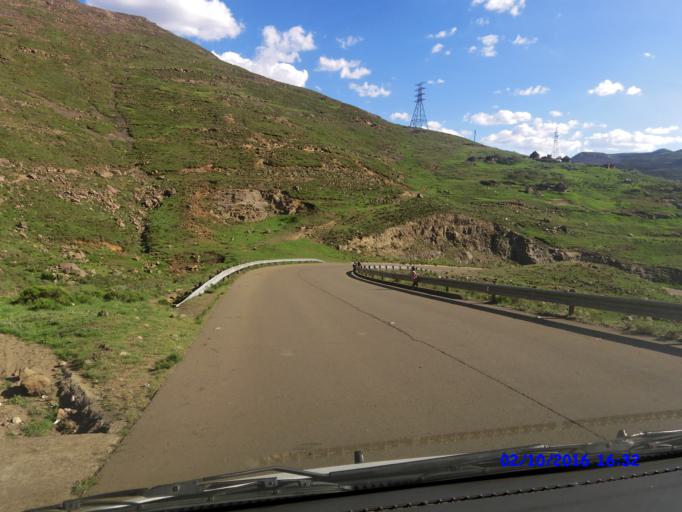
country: LS
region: Maseru
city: Nako
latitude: -29.4834
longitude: 28.0711
